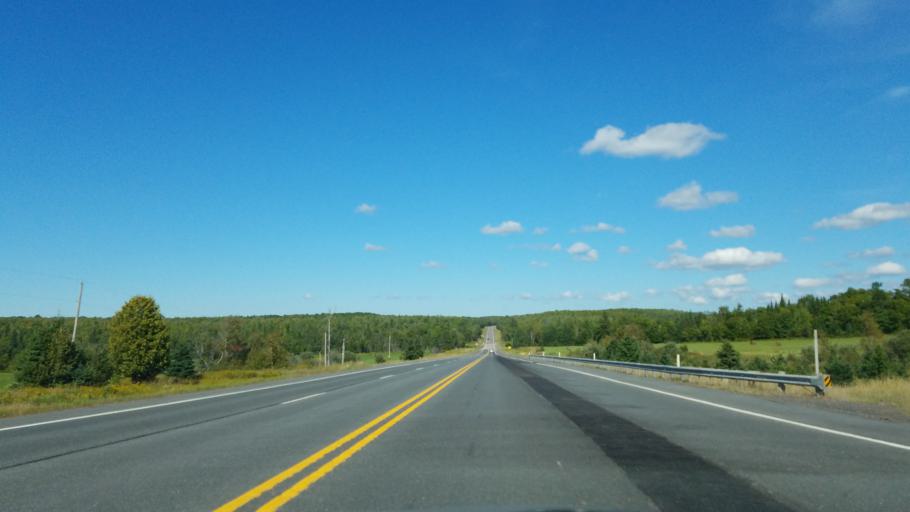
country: US
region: Michigan
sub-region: Baraga County
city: L'Anse
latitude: 46.5689
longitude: -88.4995
